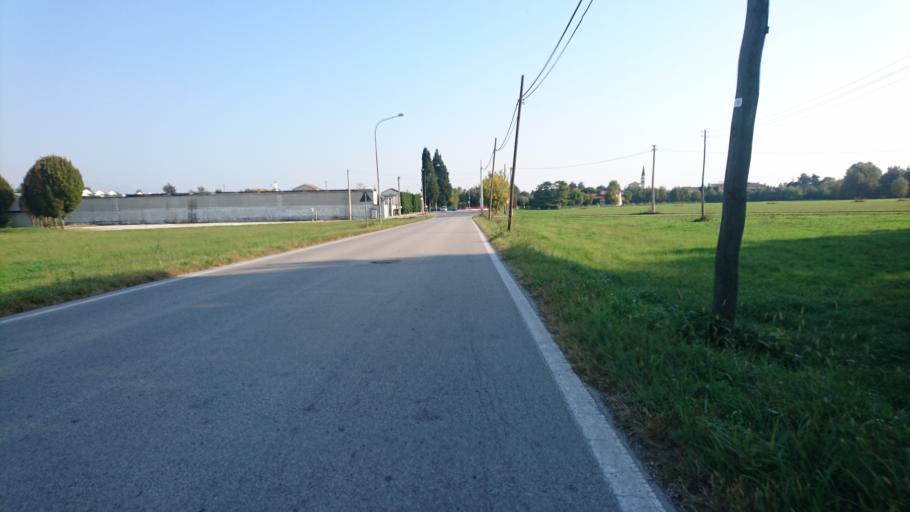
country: IT
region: Veneto
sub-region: Provincia di Padova
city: Grantorto
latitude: 45.5989
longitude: 11.7236
